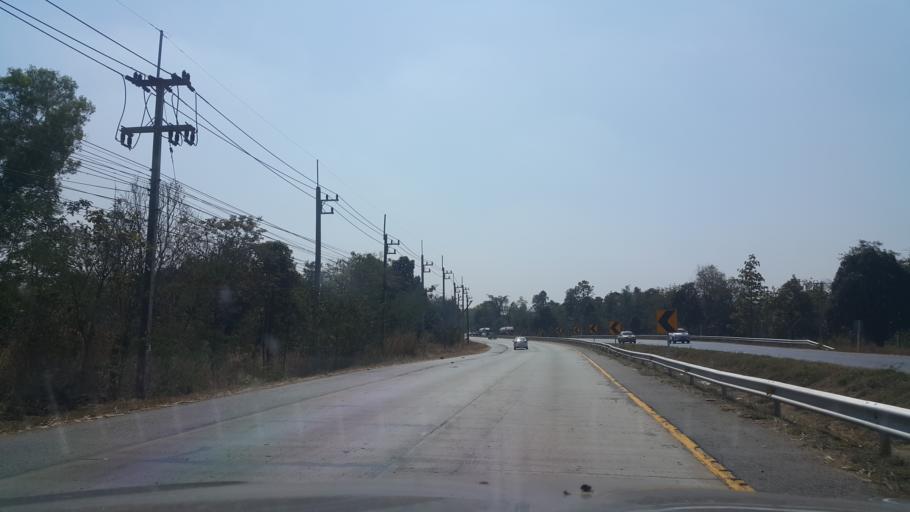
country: TH
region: Khon Kaen
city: Nam Phong
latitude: 16.8304
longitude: 102.8427
